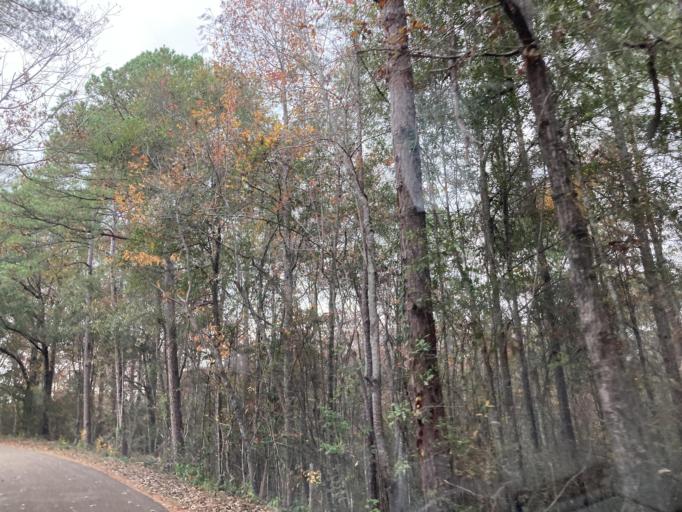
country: US
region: Mississippi
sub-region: Lamar County
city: Purvis
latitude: 31.1647
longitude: -89.6184
